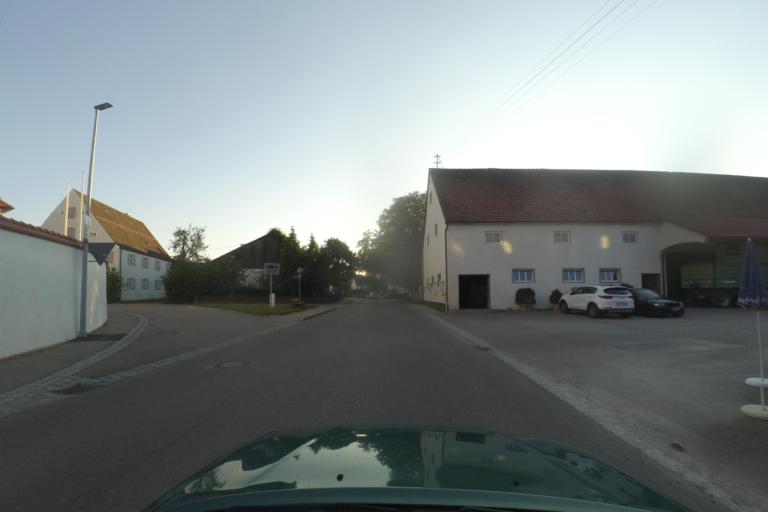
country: DE
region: Bavaria
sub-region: Upper Bavaria
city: Weil
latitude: 48.1172
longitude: 10.9221
